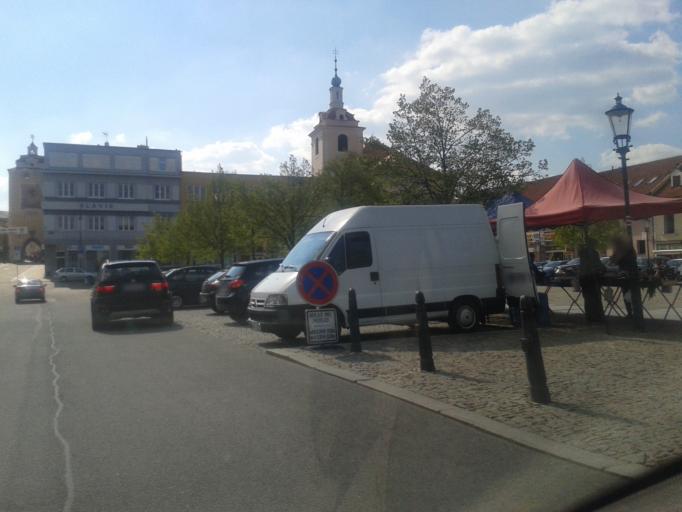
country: CZ
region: Central Bohemia
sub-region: Okres Beroun
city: Beroun
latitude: 49.9638
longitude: 14.0733
